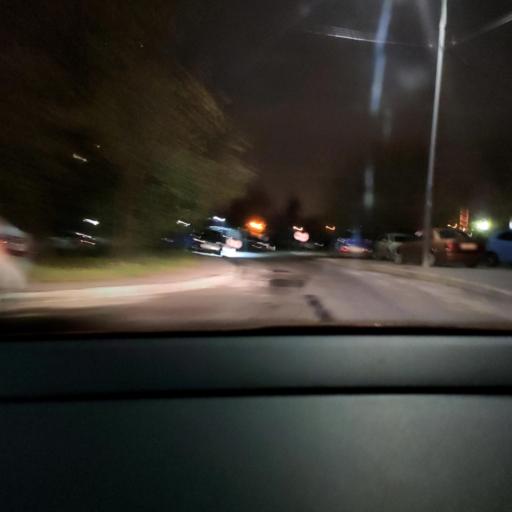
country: RU
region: Moscow
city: Strogino
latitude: 55.8066
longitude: 37.4222
